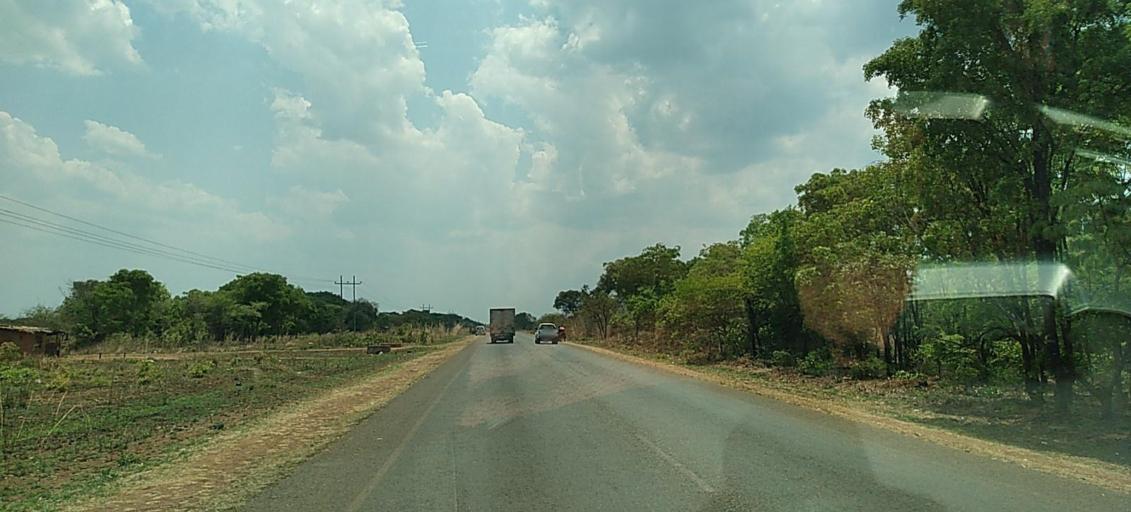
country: ZM
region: Copperbelt
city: Kalulushi
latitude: -12.8353
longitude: 27.9567
